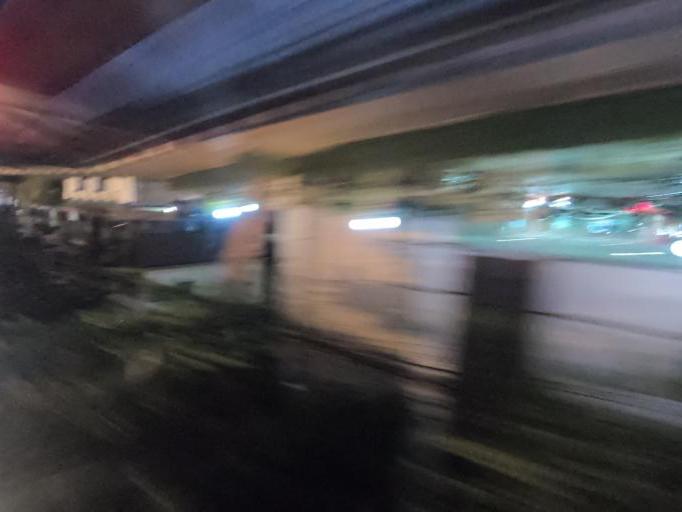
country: TH
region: Bangkok
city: Lat Phrao
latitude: 13.8001
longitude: 100.6066
